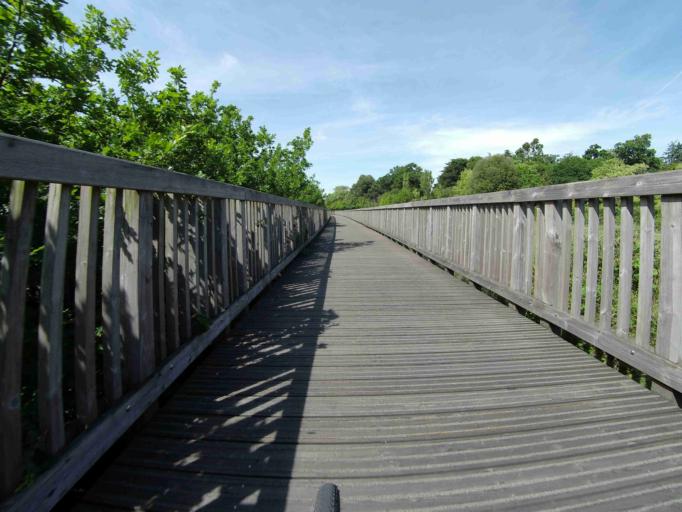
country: GB
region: England
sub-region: Devon
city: Starcross
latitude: 50.6556
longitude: -3.4356
